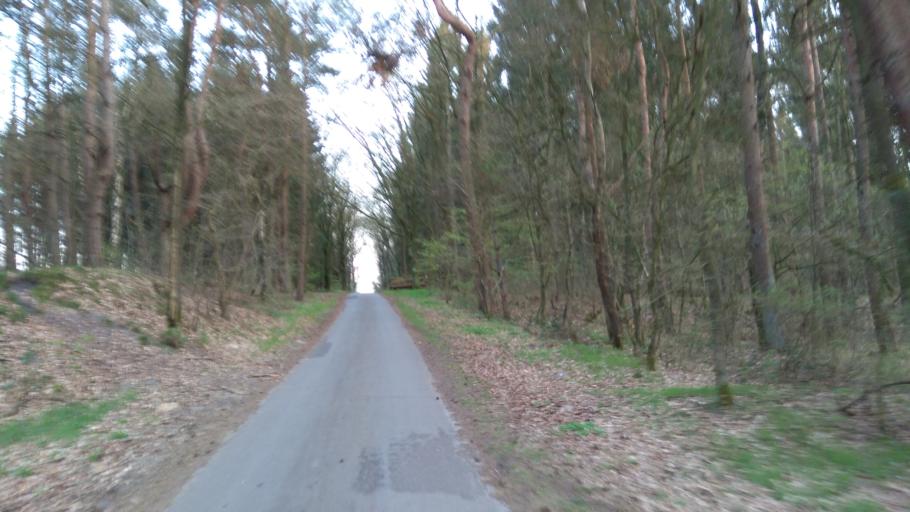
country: DE
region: Lower Saxony
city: Bargstedt
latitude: 53.4550
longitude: 9.4652
